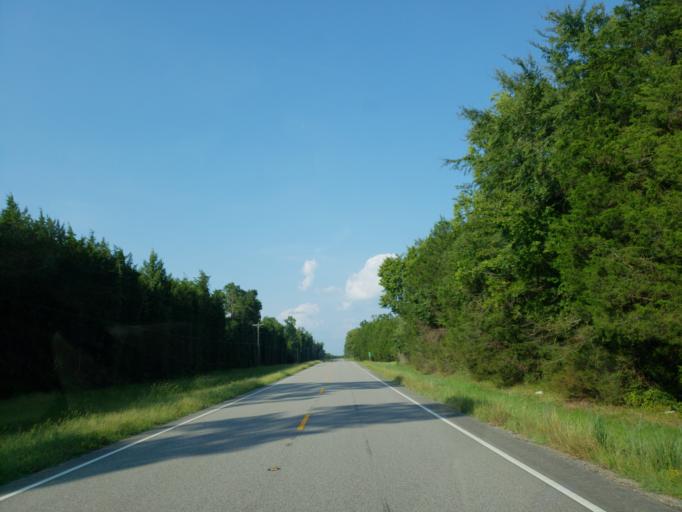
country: US
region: Alabama
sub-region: Greene County
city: Eutaw
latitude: 32.7395
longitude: -88.0519
